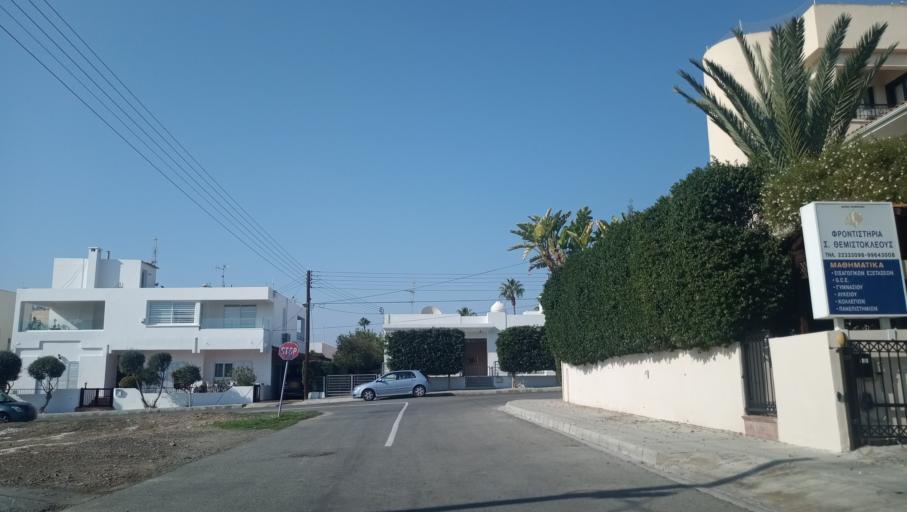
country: CY
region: Lefkosia
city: Nicosia
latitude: 35.1440
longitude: 33.3890
